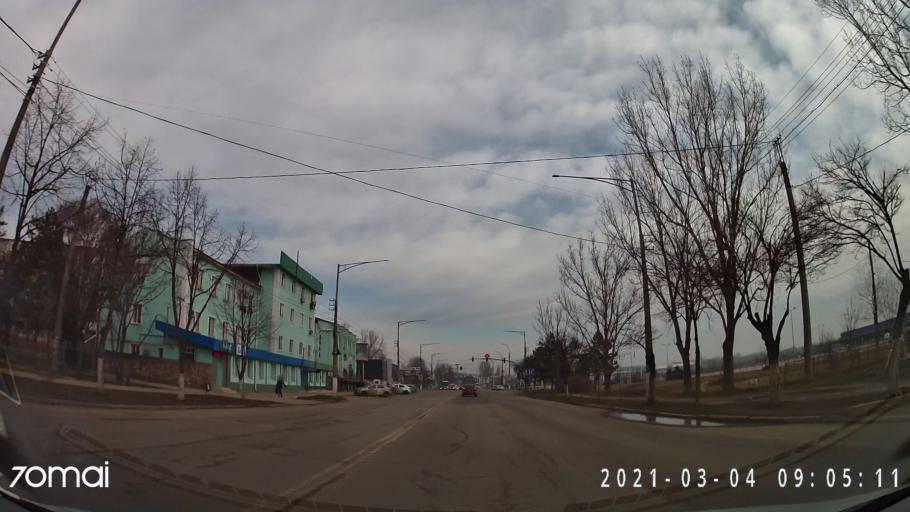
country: MD
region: Balti
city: Balti
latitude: 47.7645
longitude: 27.9414
